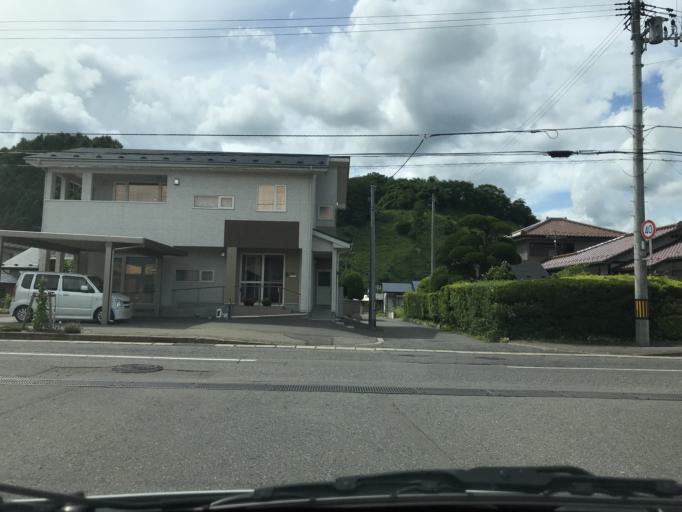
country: JP
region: Iwate
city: Tono
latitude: 39.3244
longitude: 141.5321
